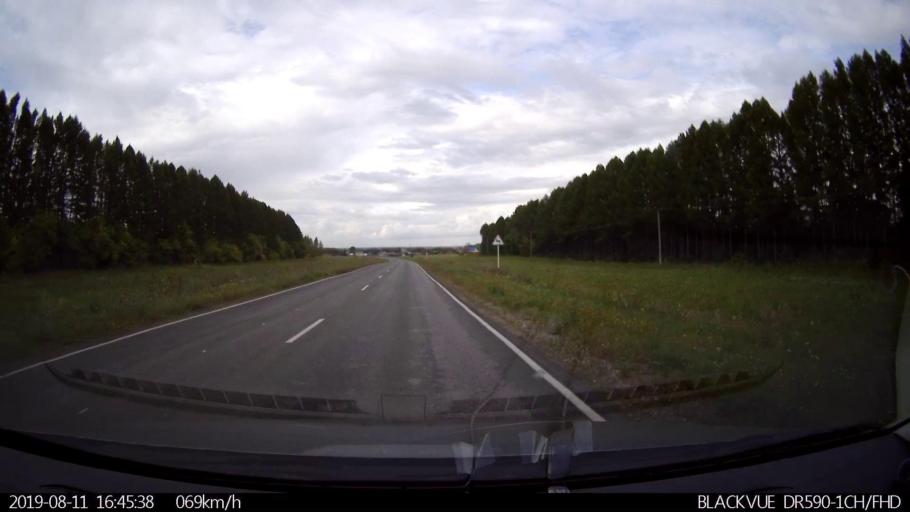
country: RU
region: Ulyanovsk
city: Mayna
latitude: 54.1918
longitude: 47.6872
